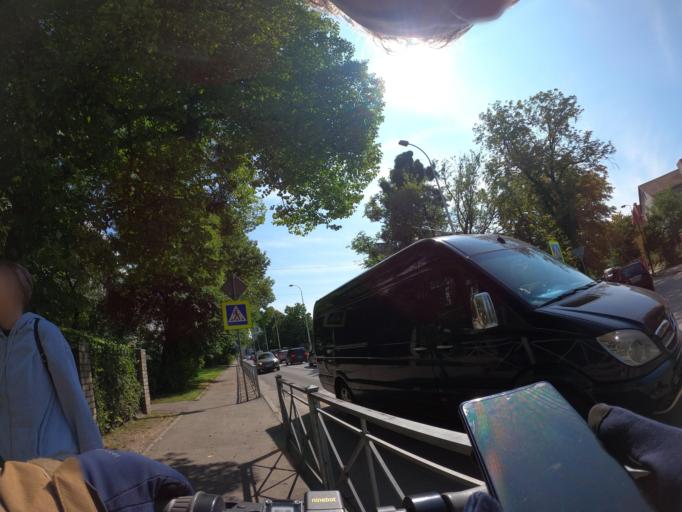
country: RU
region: Kaliningrad
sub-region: Gorod Kaliningrad
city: Kaliningrad
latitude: 54.7353
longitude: 20.5275
